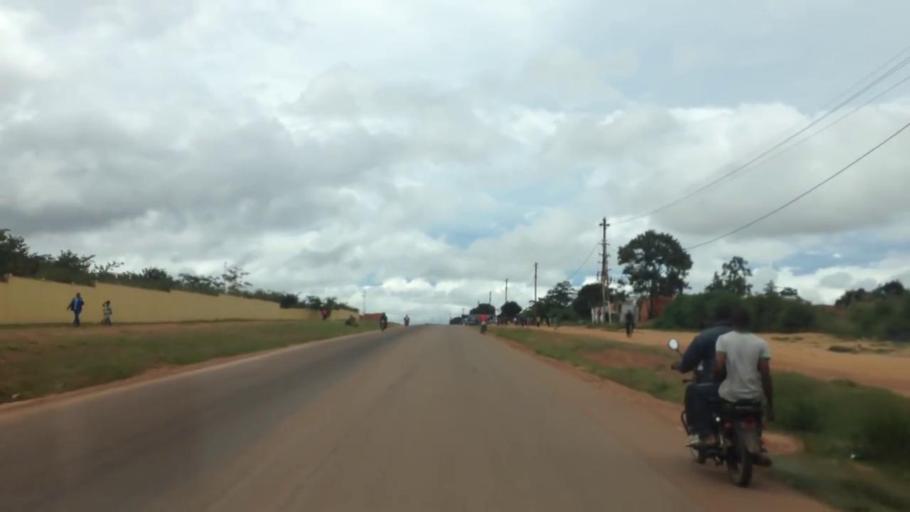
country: CD
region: Katanga
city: Kolwezi
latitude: -10.7266
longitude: 25.5090
